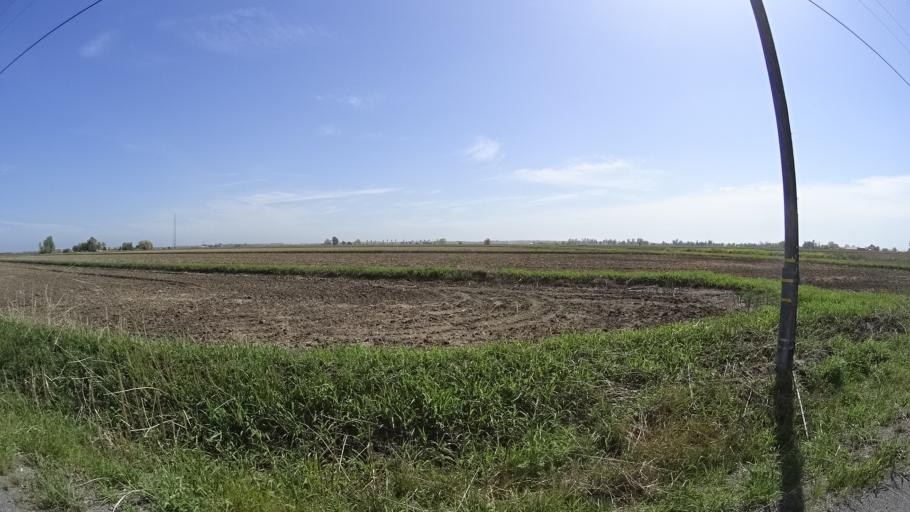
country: US
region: California
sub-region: Glenn County
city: Willows
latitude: 39.5910
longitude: -122.0559
